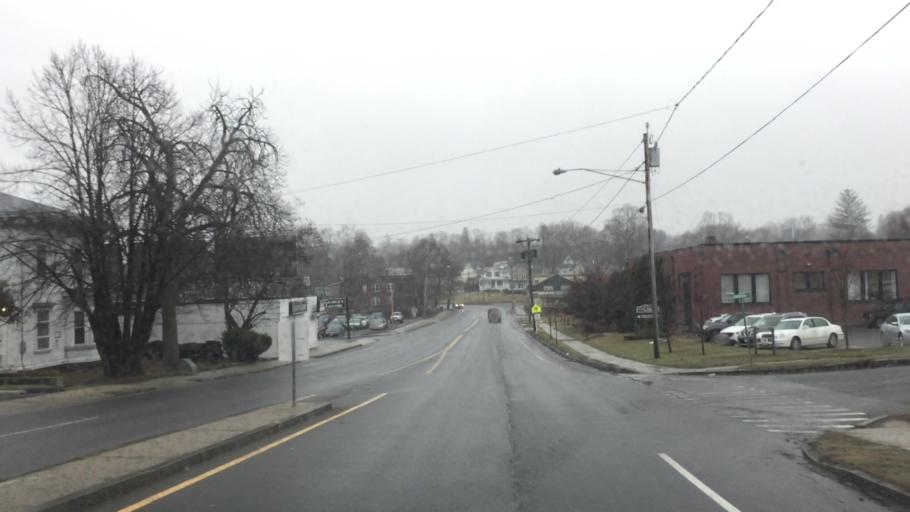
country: US
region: Massachusetts
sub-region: Berkshire County
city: Pittsfield
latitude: 42.4466
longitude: -73.2450
